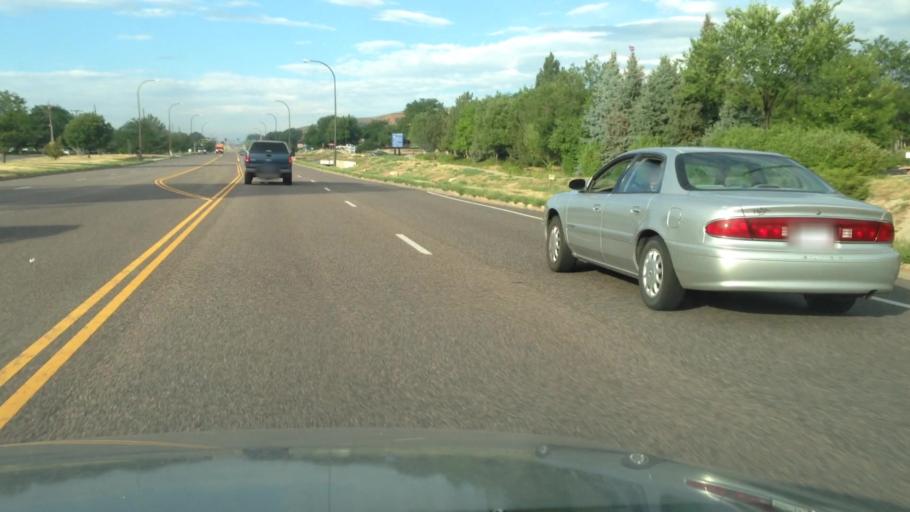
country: US
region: Colorado
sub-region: Jefferson County
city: West Pleasant View
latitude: 39.7067
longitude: -105.1363
